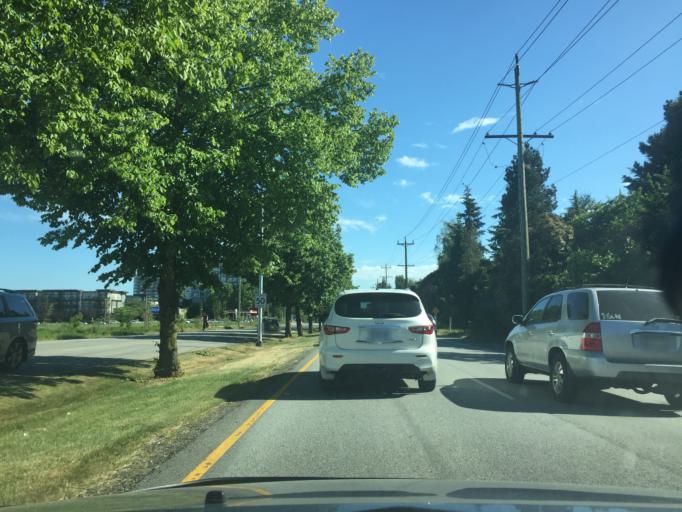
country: CA
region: British Columbia
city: Richmond
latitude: 49.1723
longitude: -123.1247
